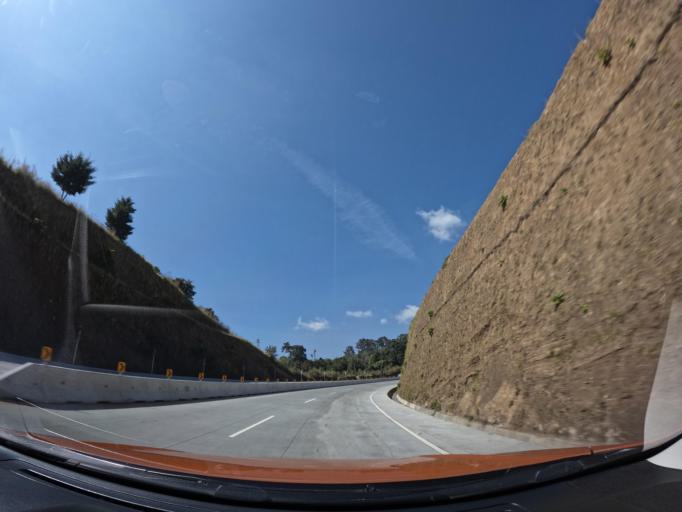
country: GT
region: Guatemala
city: Villa Canales
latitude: 14.4928
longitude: -90.5259
